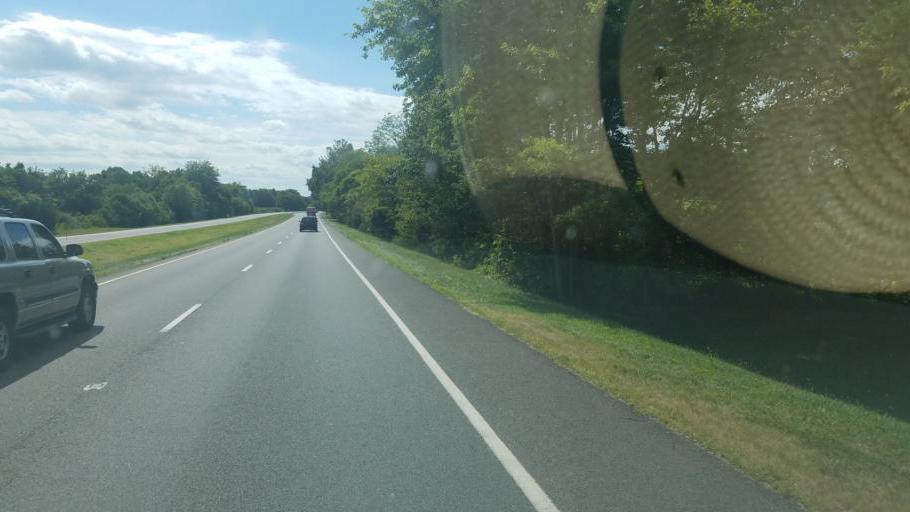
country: US
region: Virginia
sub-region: Fauquier County
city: Bealeton
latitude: 38.6044
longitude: -77.7818
